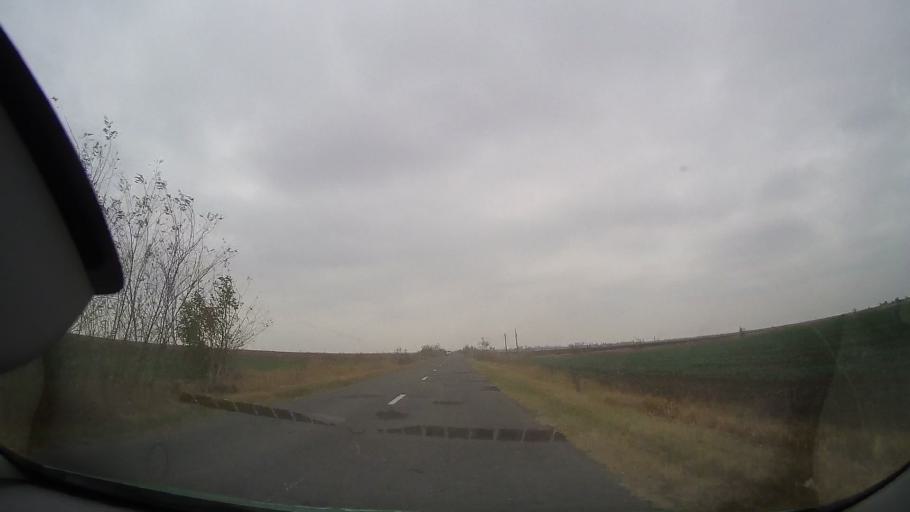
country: RO
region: Ialomita
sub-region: Comuna Valea Macrisului
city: Valea Macrisului
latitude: 44.7577
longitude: 26.8050
